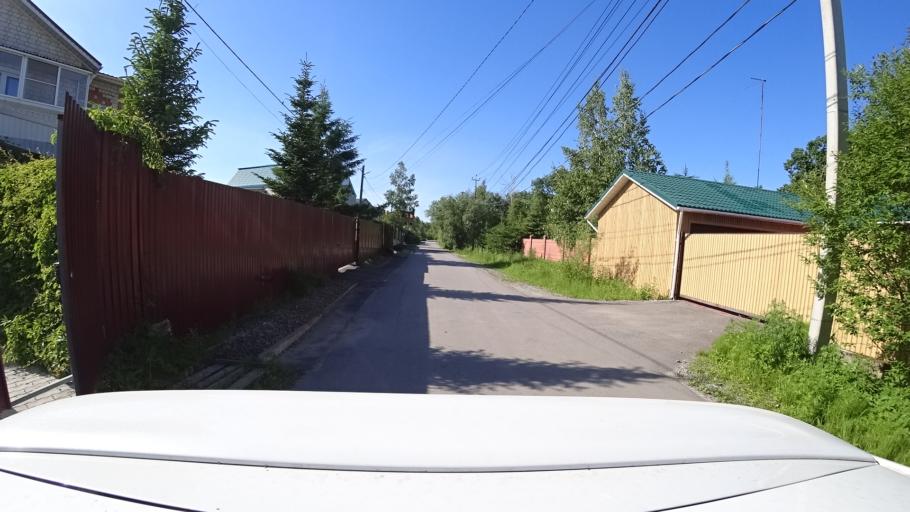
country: RU
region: Khabarovsk Krai
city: Topolevo
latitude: 48.5426
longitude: 135.1792
